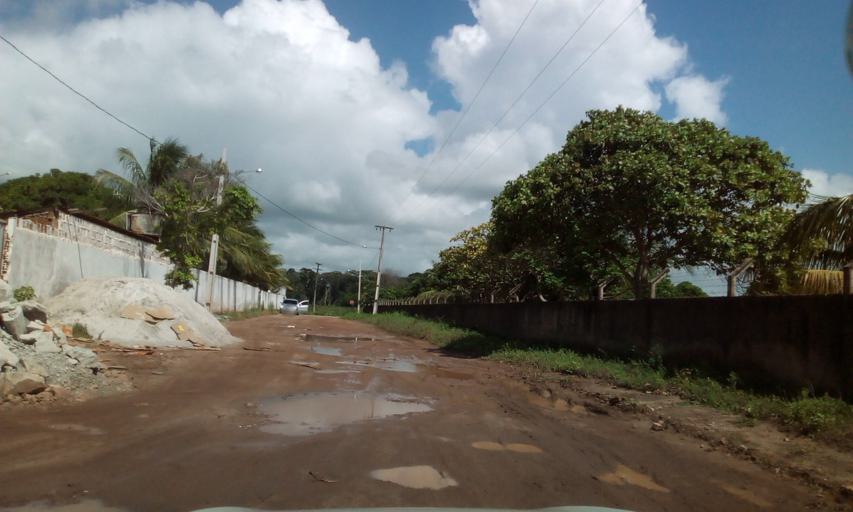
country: BR
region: Paraiba
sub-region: Conde
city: Conde
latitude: -7.2229
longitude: -34.8229
